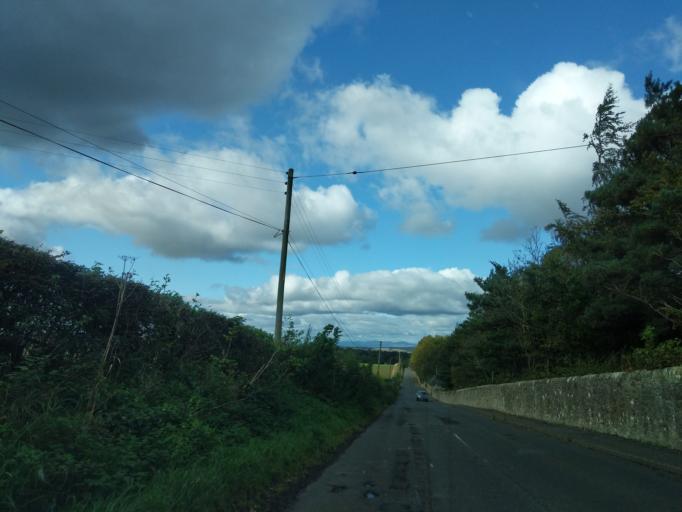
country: GB
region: Scotland
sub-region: Edinburgh
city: Currie
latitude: 55.9047
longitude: -3.3261
